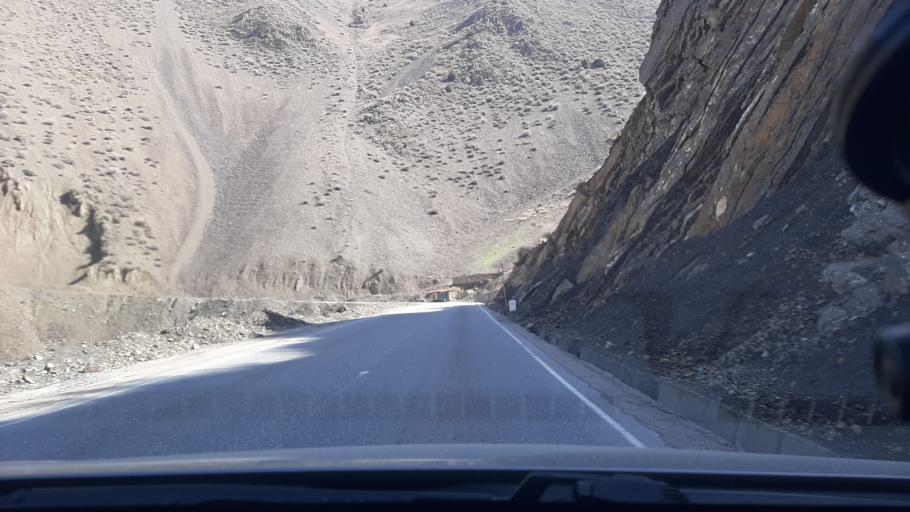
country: TJ
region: Viloyati Sughd
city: Ayni
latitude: 39.4589
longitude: 68.5573
